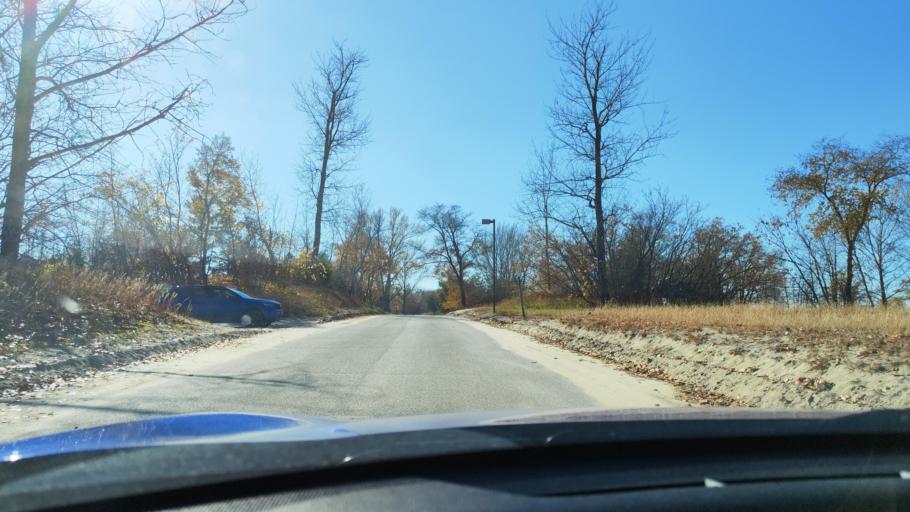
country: CA
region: Ontario
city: Wasaga Beach
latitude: 44.5283
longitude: -80.0146
